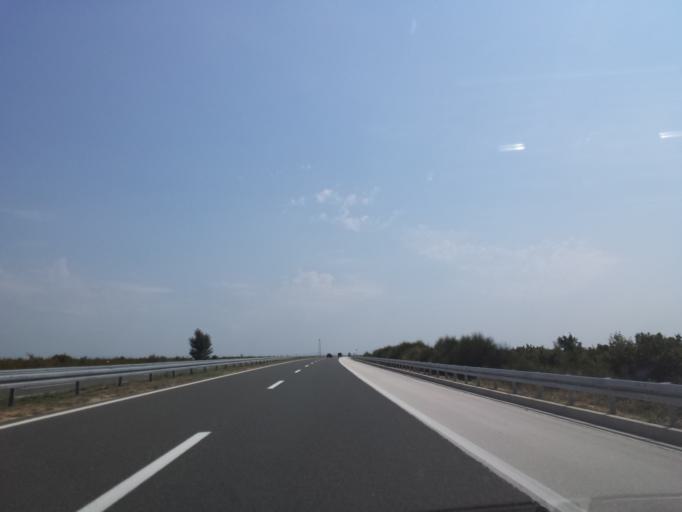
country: HR
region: Sibensko-Kniniska
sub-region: Grad Sibenik
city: Pirovac
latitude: 43.9198
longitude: 15.7390
